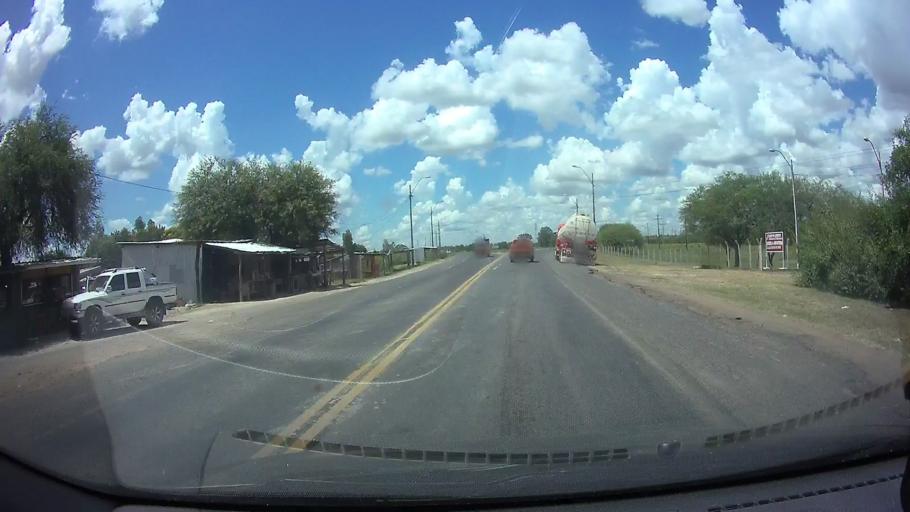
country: PY
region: Central
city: Colonia Mariano Roque Alonso
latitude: -25.1722
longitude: -57.5683
